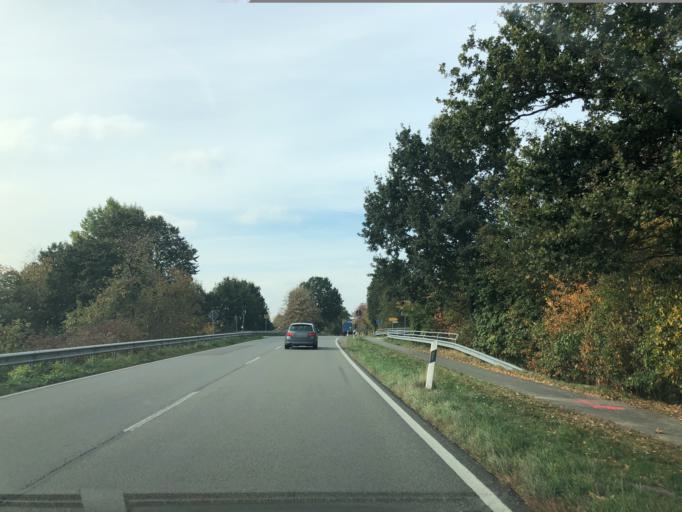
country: DE
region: Lower Saxony
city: Surwold
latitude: 53.0126
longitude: 7.5268
